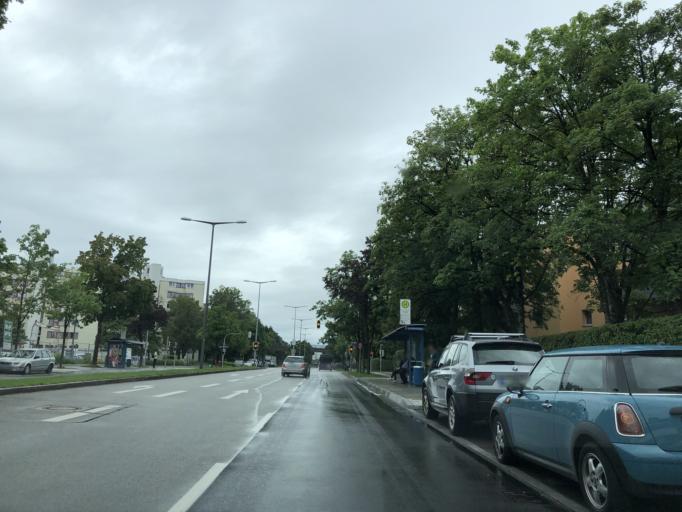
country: DE
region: Bavaria
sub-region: Upper Bavaria
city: Neubiberg
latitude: 48.0993
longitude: 11.6575
